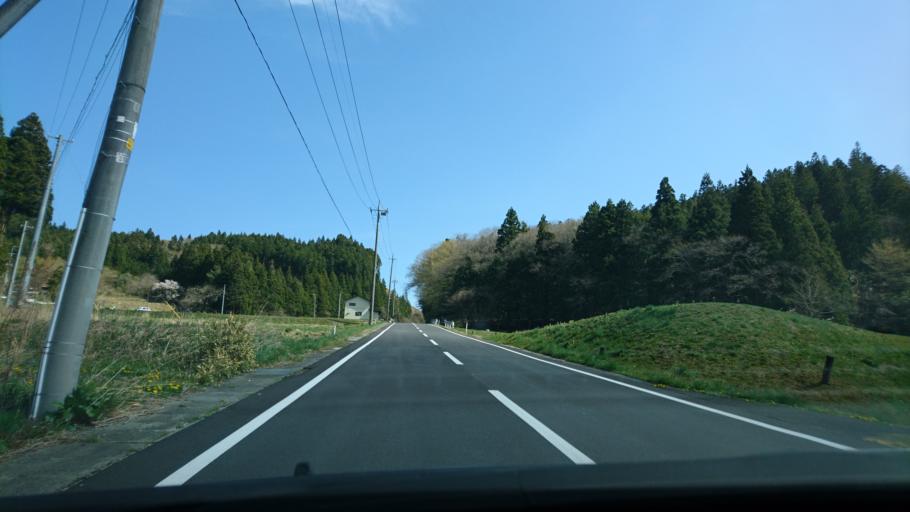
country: JP
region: Iwate
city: Ofunato
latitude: 38.9329
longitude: 141.4506
